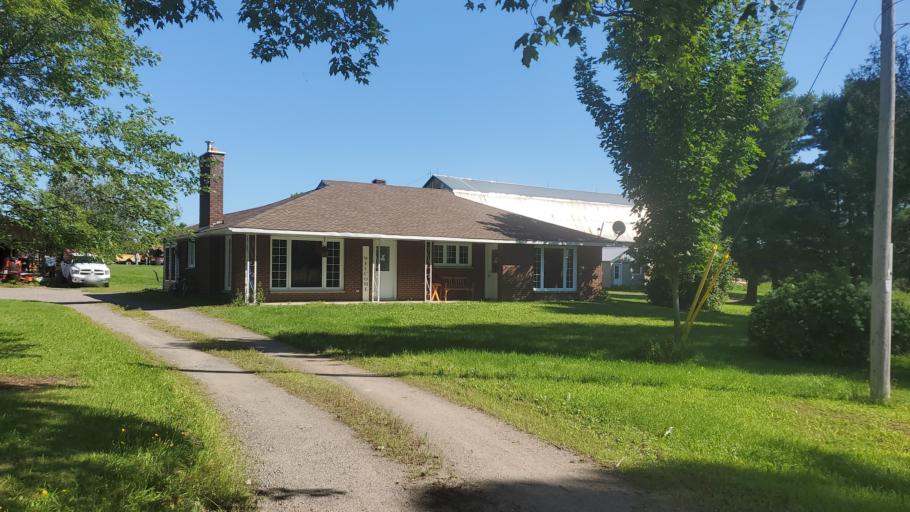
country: CA
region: Ontario
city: Powassan
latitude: 46.2166
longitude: -79.2382
